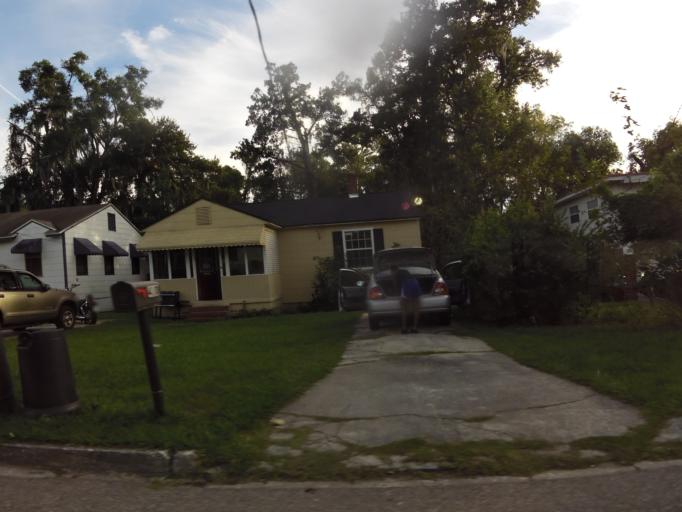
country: US
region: Florida
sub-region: Duval County
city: Jacksonville
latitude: 30.3844
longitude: -81.6593
